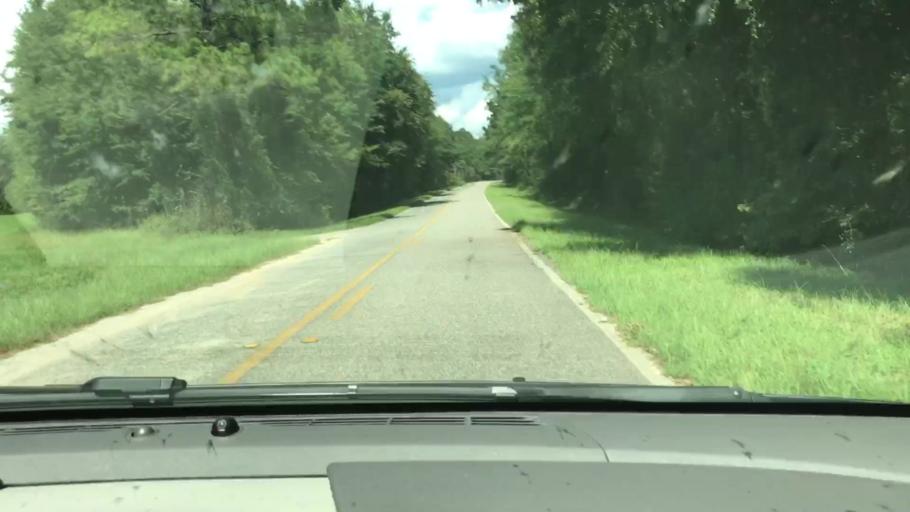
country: US
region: Georgia
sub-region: Clay County
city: Fort Gaines
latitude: 31.7342
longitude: -85.0921
